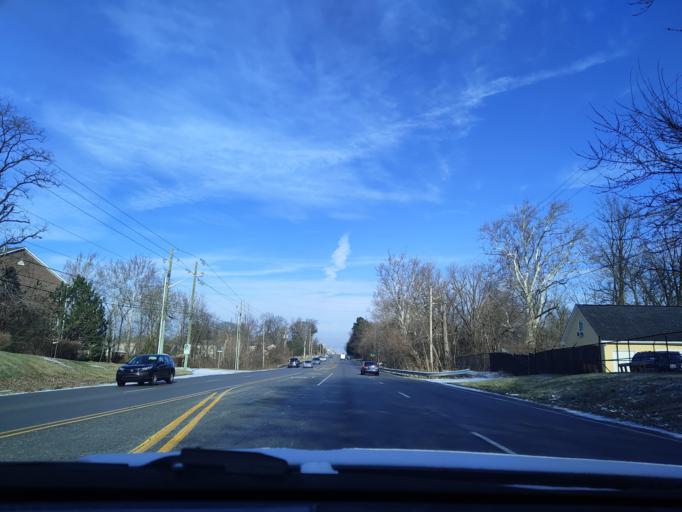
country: US
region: Indiana
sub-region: Marion County
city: Meridian Hills
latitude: 39.8997
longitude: -86.2169
